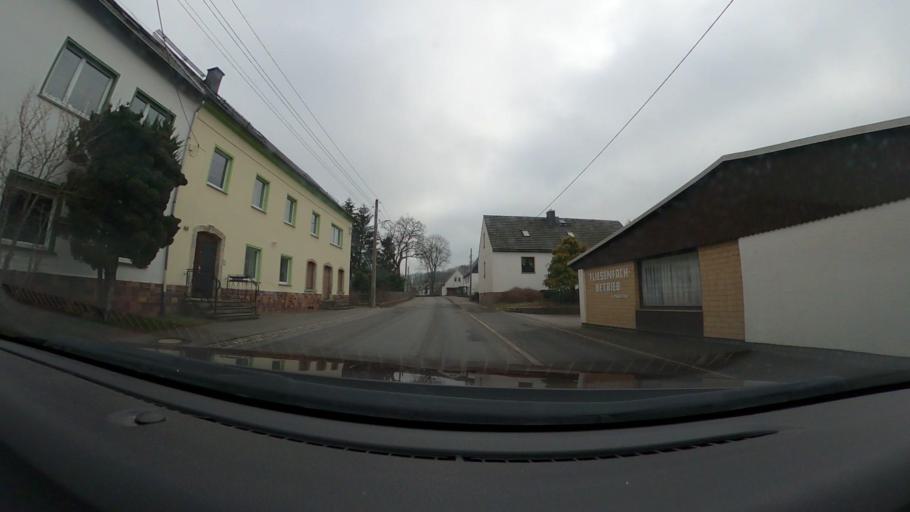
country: DE
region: Saxony
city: Oberschona
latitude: 50.8942
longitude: 13.2586
